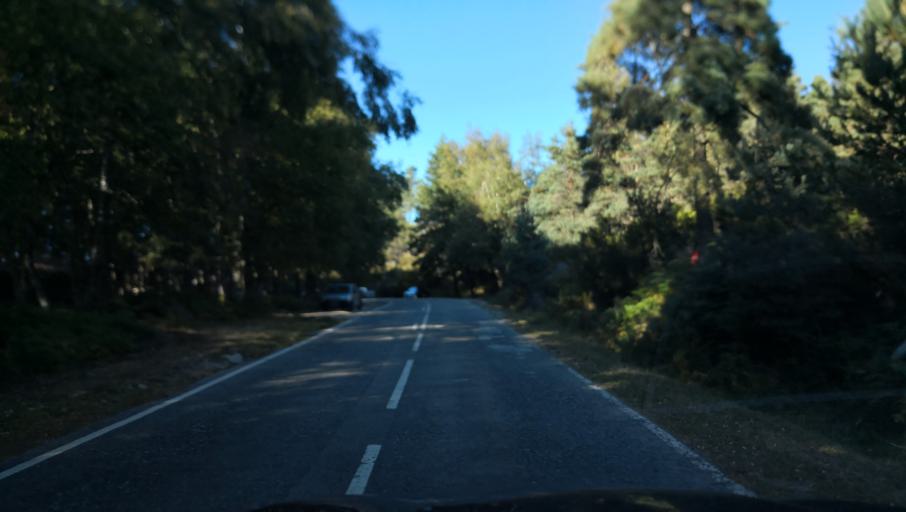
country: PT
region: Vila Real
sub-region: Vila Real
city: Vila Real
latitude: 41.3480
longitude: -7.7905
